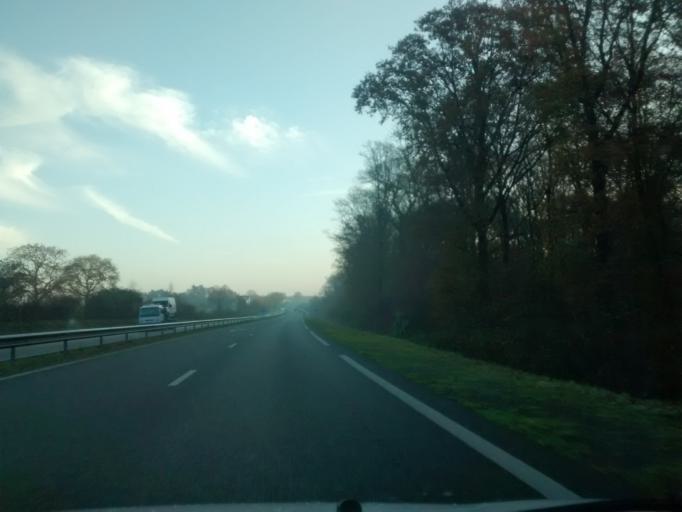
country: FR
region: Brittany
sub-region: Departement d'Ille-et-Vilaine
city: Chasne-sur-Illet
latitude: 48.2852
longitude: -1.5923
